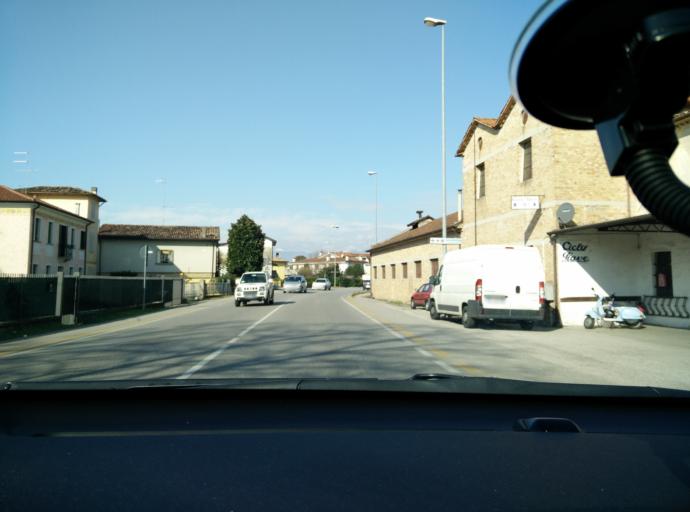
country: IT
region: Veneto
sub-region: Provincia di Treviso
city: Santa Lucia di Piave
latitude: 45.8503
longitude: 12.3092
